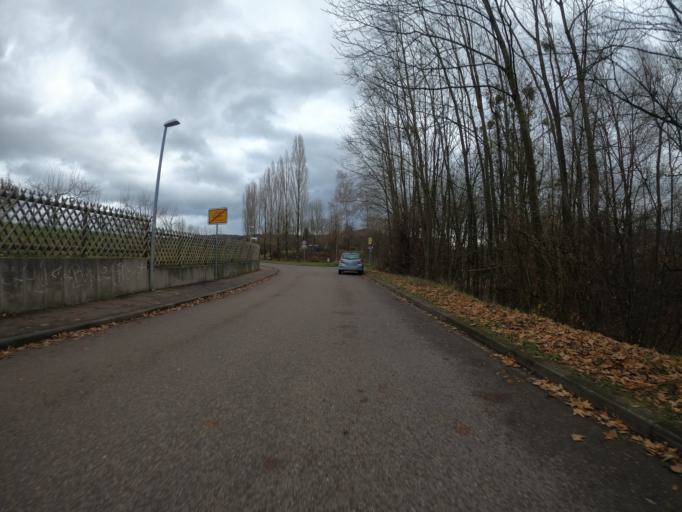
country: DE
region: Baden-Wuerttemberg
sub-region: Regierungsbezirk Stuttgart
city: Sussen
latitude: 48.6781
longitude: 9.7663
